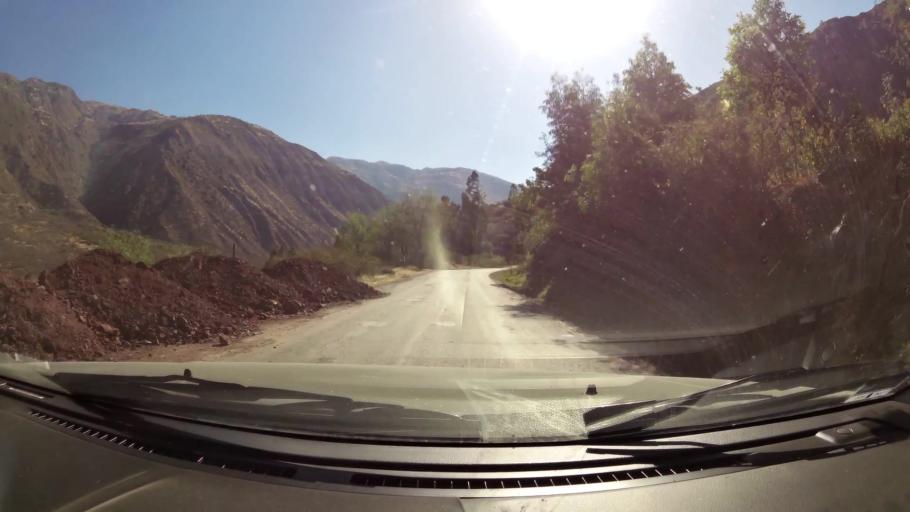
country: PE
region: Huancavelica
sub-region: Provincia de Acobamba
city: Pomacocha
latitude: -12.7634
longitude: -74.5153
